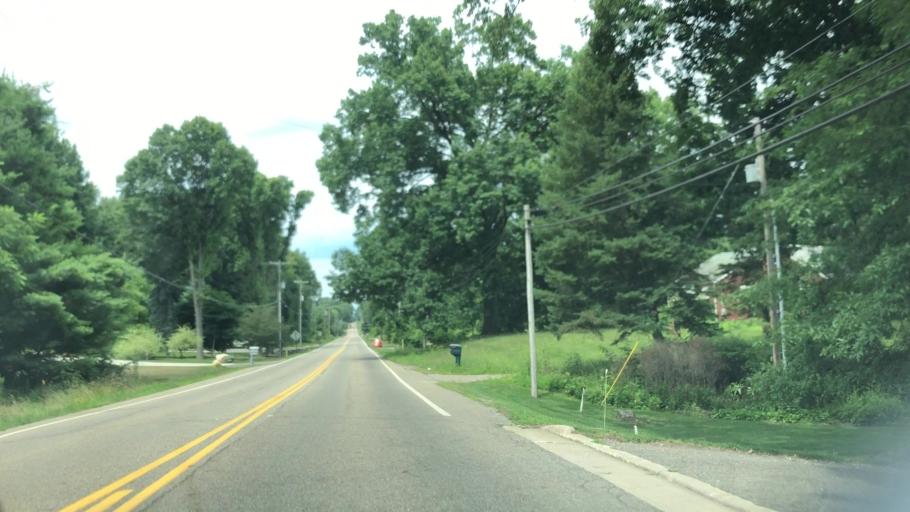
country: US
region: Ohio
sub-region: Summit County
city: Greensburg
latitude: 40.8798
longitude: -81.4600
